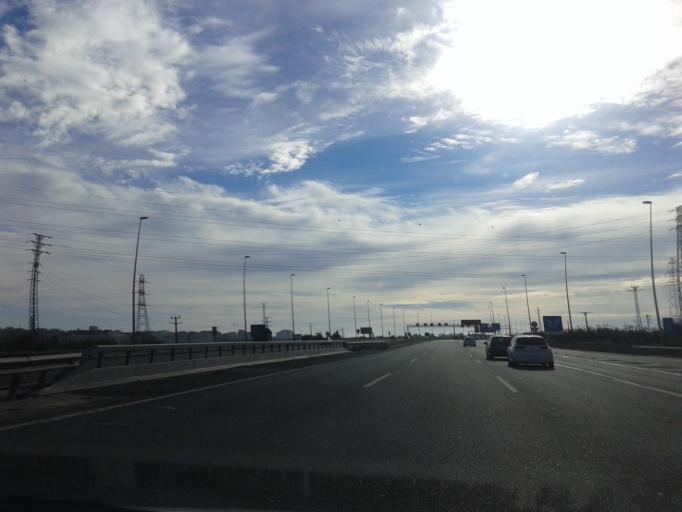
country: ES
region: Catalonia
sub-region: Provincia de Barcelona
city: Sant Vicenc dels Horts
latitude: 41.3906
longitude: 2.0254
